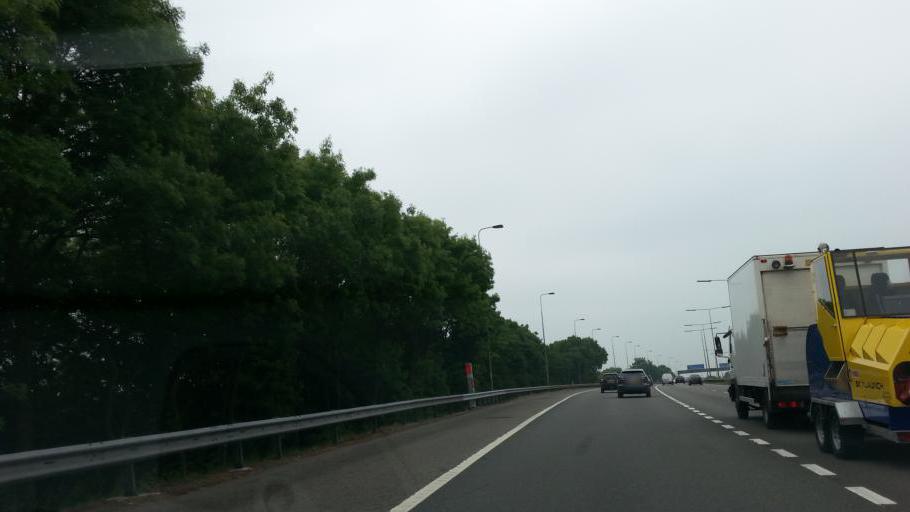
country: GB
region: England
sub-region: Warwickshire
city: Brandon
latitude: 52.4393
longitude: -1.4239
